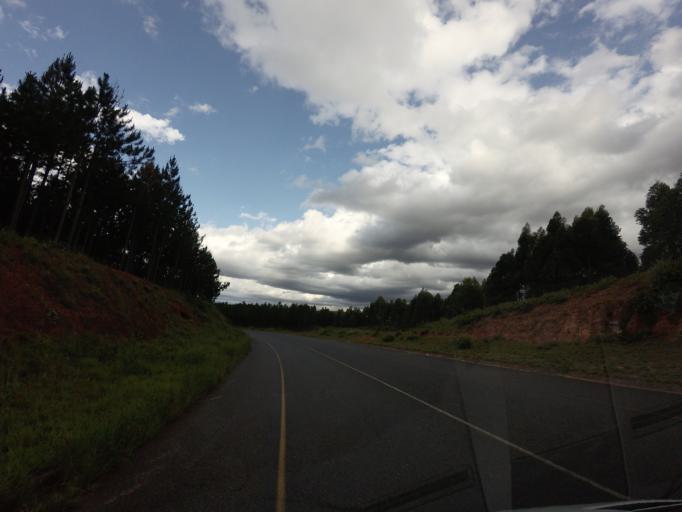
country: ZA
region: Mpumalanga
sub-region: Ehlanzeni District
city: Graksop
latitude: -24.9923
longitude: 31.0067
